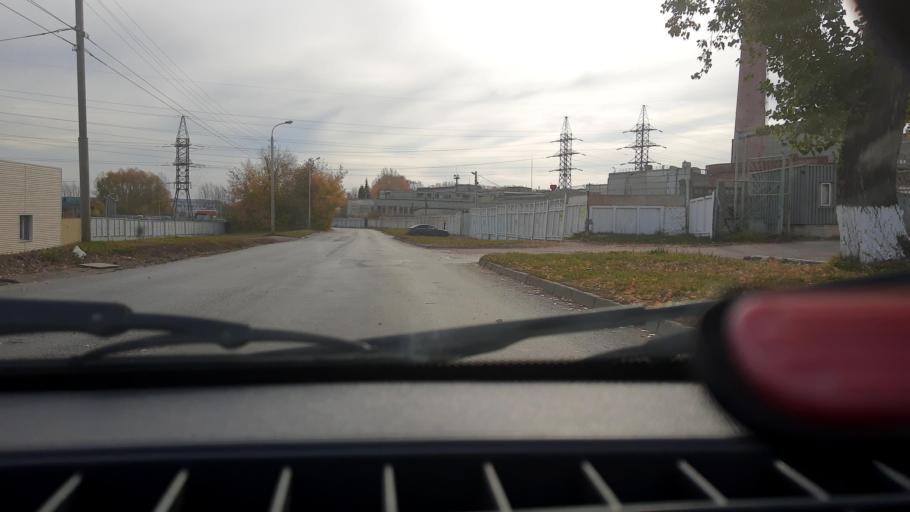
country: RU
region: Bashkortostan
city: Avdon
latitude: 54.6878
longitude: 55.8092
